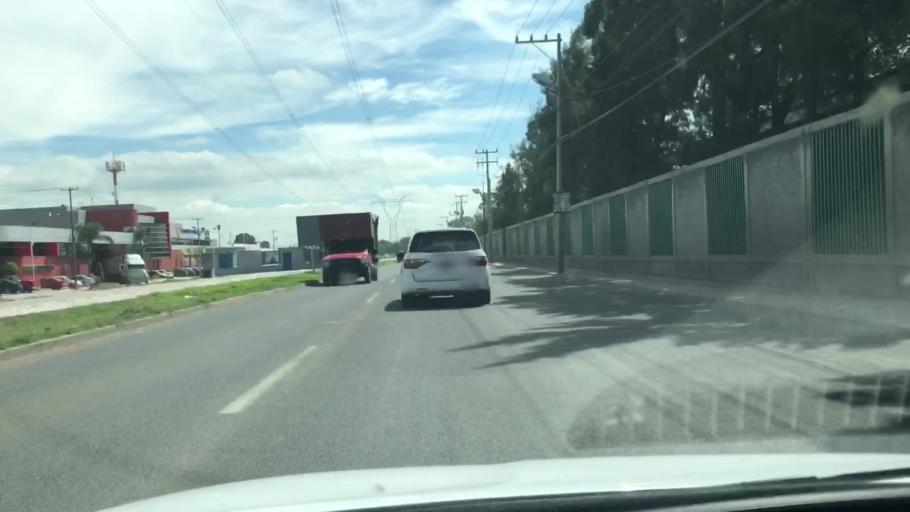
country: MX
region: Guanajuato
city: Celaya
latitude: 20.5522
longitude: -100.8197
